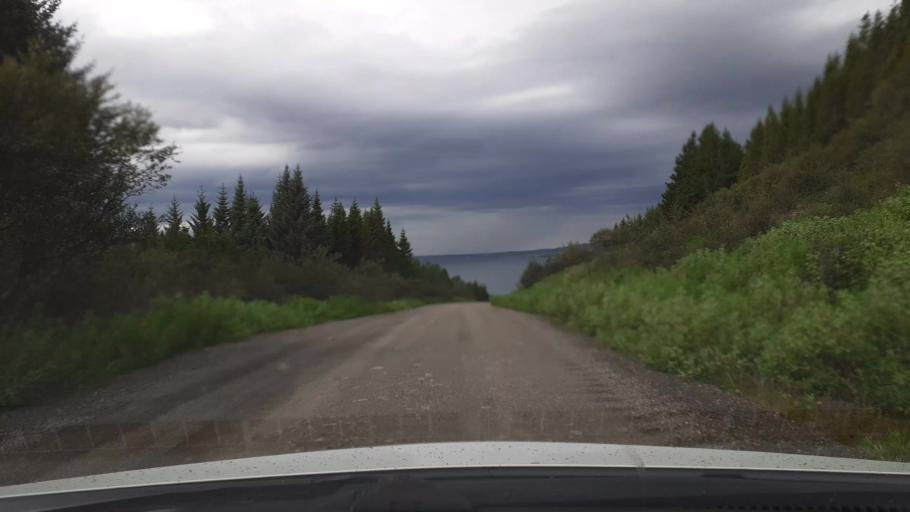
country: IS
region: Capital Region
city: Mosfellsbaer
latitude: 64.5279
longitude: -21.5025
